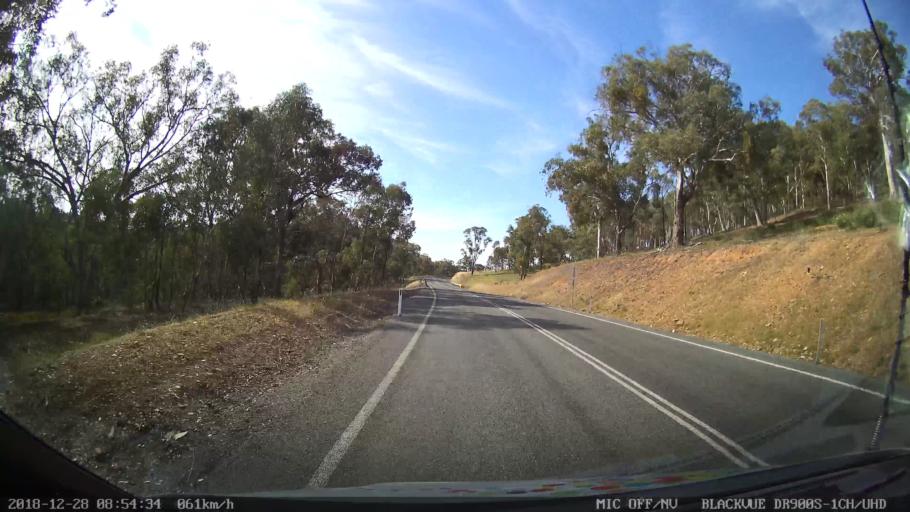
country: AU
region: New South Wales
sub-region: Upper Lachlan Shire
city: Crookwell
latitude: -34.0931
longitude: 149.3322
